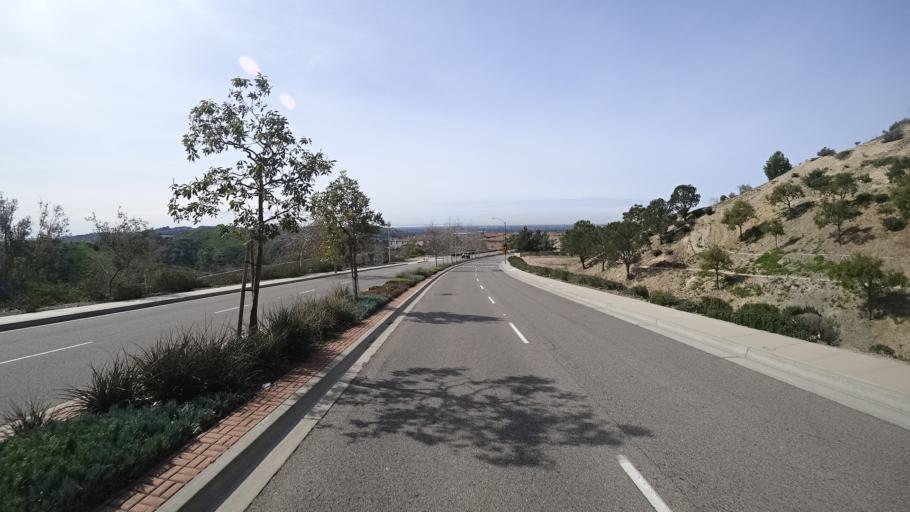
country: US
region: California
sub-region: Orange County
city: Villa Park
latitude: 33.8270
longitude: -117.7707
